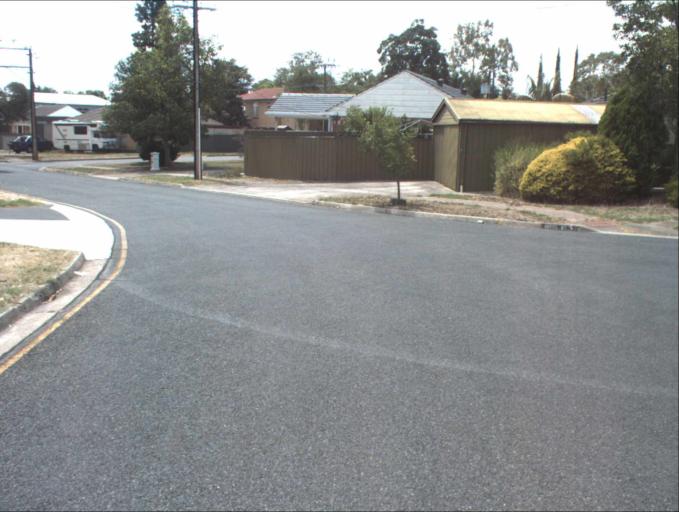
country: AU
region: South Australia
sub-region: Tea Tree Gully
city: Modbury
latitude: -34.8397
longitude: 138.6665
